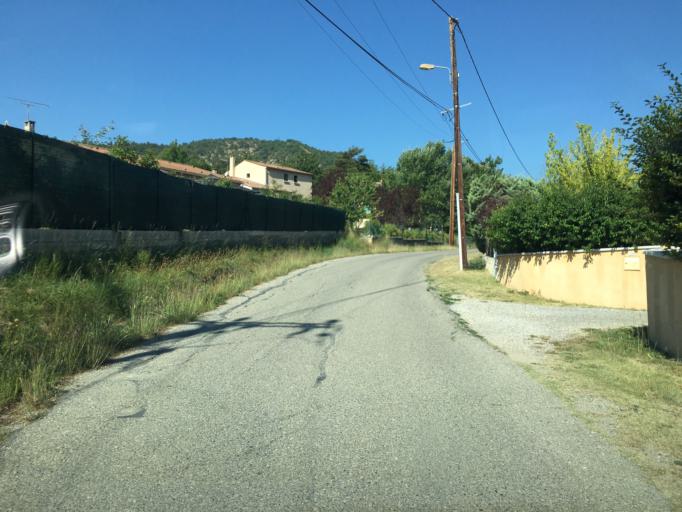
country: FR
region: Provence-Alpes-Cote d'Azur
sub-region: Departement des Alpes-de-Haute-Provence
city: Mallemoisson
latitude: 44.0667
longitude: 6.1403
